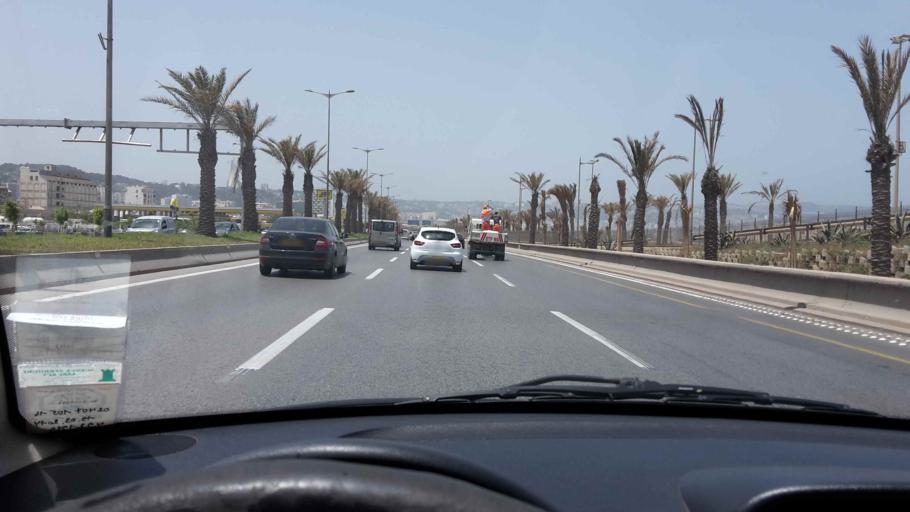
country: DZ
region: Alger
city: Algiers
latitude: 36.7457
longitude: 3.1007
